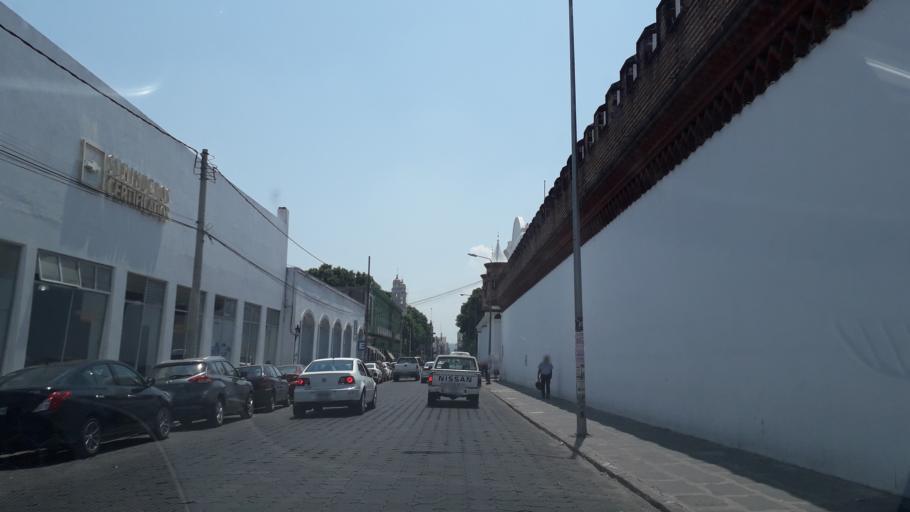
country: MX
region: Puebla
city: Puebla
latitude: 19.0494
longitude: -98.2085
